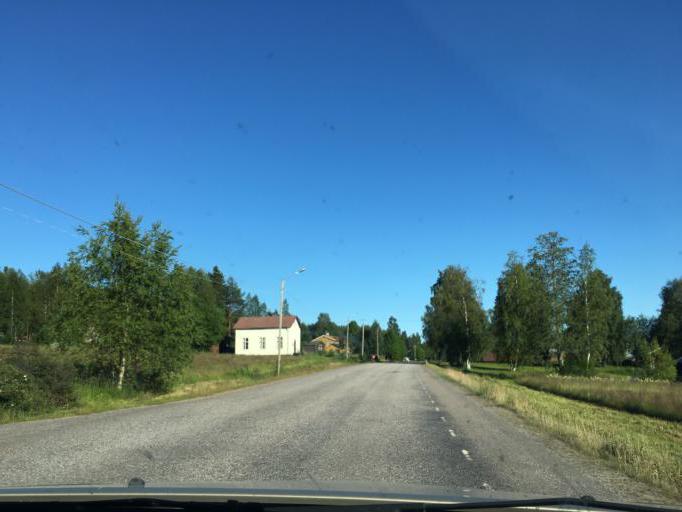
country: SE
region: Norrbotten
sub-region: Kalix Kommun
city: Rolfs
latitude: 65.9238
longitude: 22.9082
